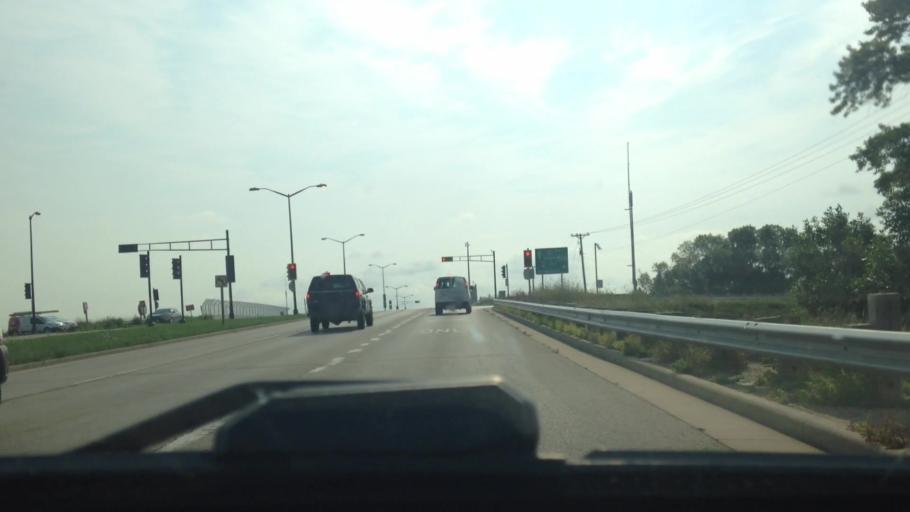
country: US
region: Wisconsin
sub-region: Fond du Lac County
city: North Fond du Lac
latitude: 43.7844
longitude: -88.4845
